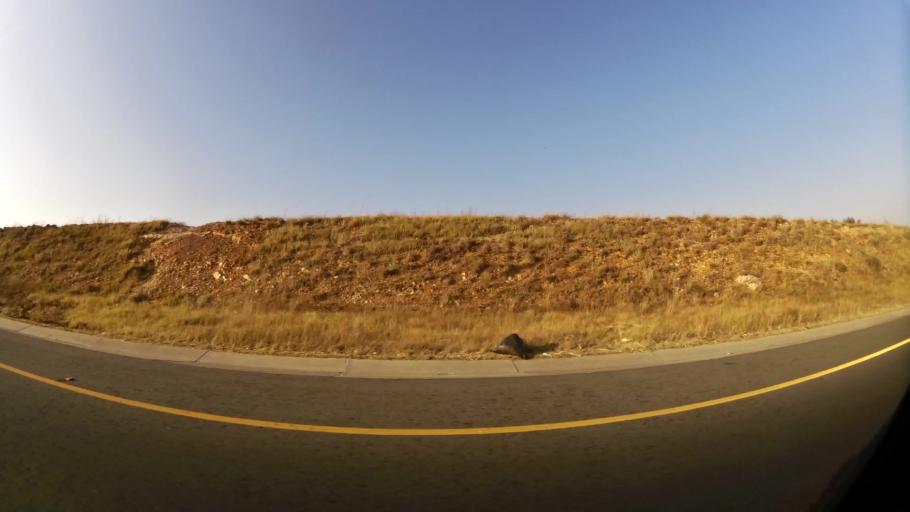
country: ZA
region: Gauteng
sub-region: City of Johannesburg Metropolitan Municipality
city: Roodepoort
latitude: -26.2188
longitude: 27.9430
